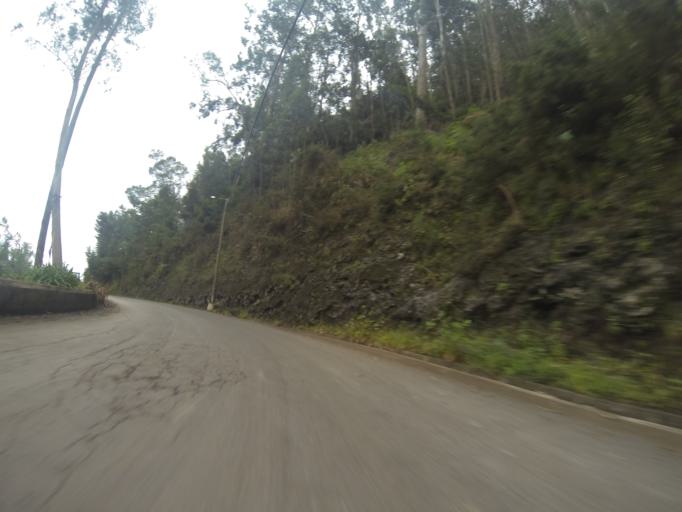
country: PT
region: Madeira
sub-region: Camara de Lobos
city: Curral das Freiras
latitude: 32.6841
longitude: -16.9539
